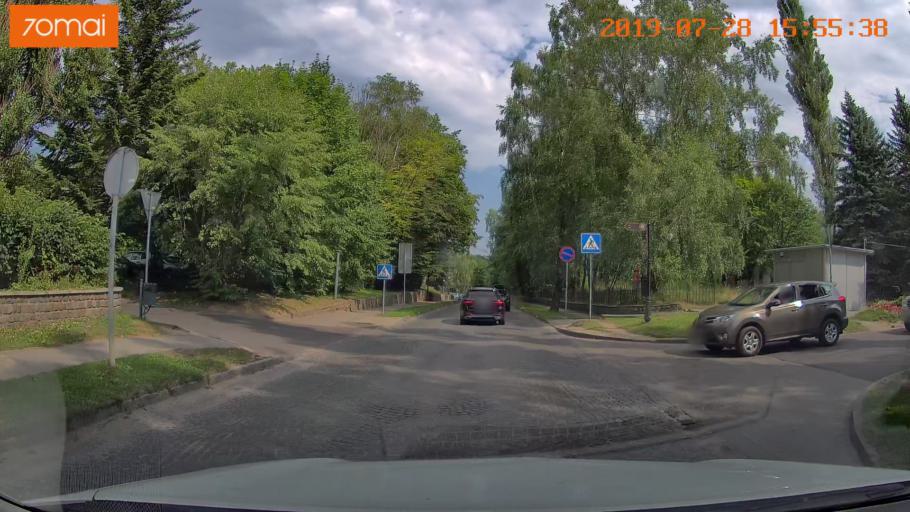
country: RU
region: Kaliningrad
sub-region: Gorod Svetlogorsk
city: Svetlogorsk
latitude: 54.9408
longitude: 20.1410
